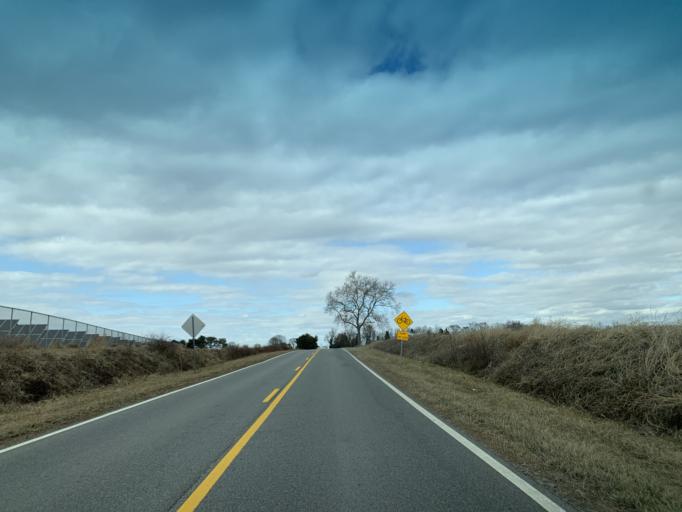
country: US
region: Maryland
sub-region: Queen Anne's County
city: Centreville
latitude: 38.9458
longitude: -76.0798
